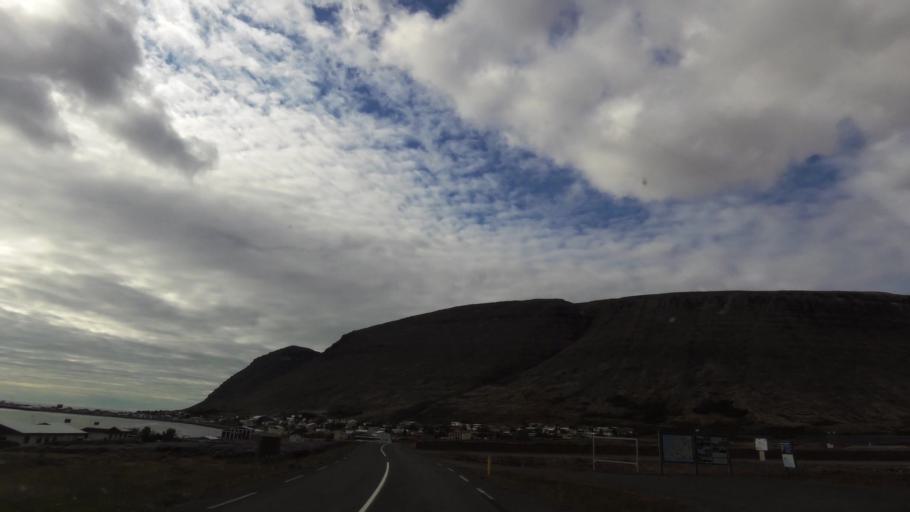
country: IS
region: West
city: Olafsvik
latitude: 65.5887
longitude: -23.9704
